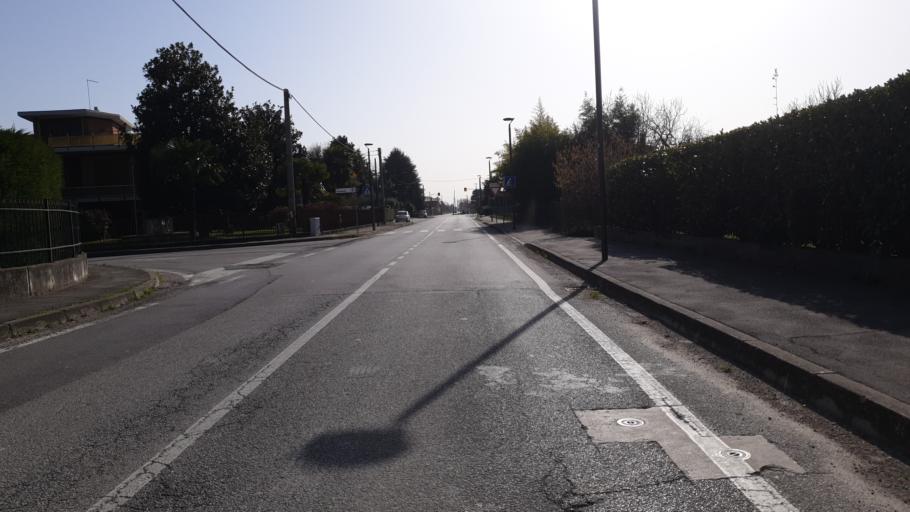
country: IT
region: Veneto
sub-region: Provincia di Padova
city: Cavino
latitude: 45.5159
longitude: 11.8837
